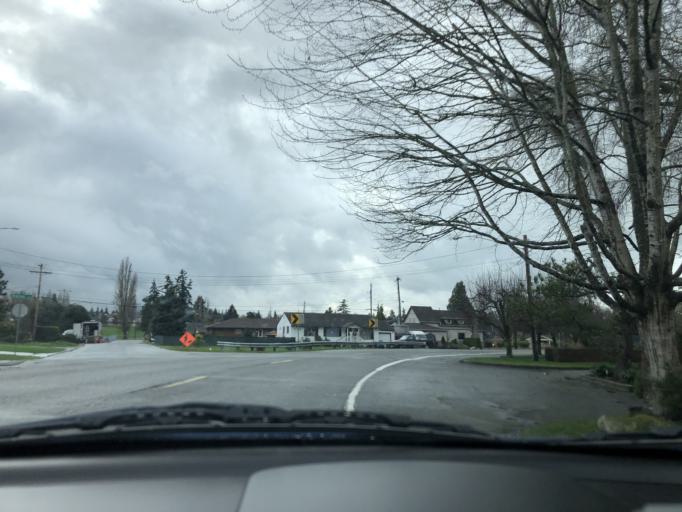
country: US
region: Washington
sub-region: Snohomish County
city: Everett
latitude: 48.0131
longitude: -122.2050
